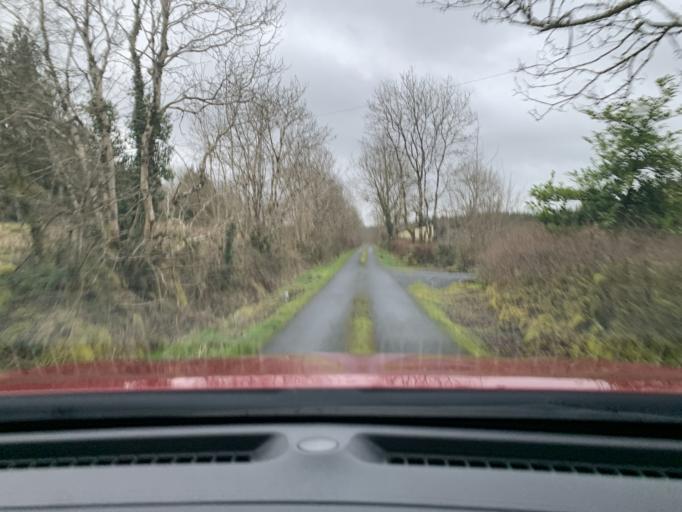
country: IE
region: Connaught
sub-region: Roscommon
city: Boyle
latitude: 54.0048
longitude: -8.3791
